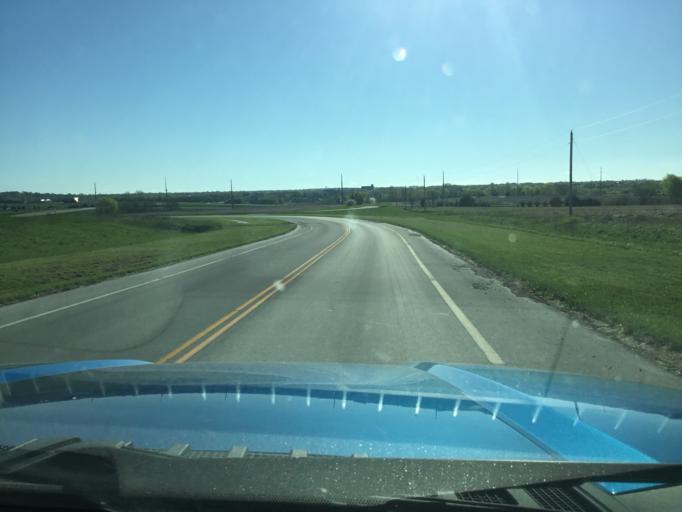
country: US
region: Kansas
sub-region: Douglas County
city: Lawrence
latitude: 38.9569
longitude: -95.3431
